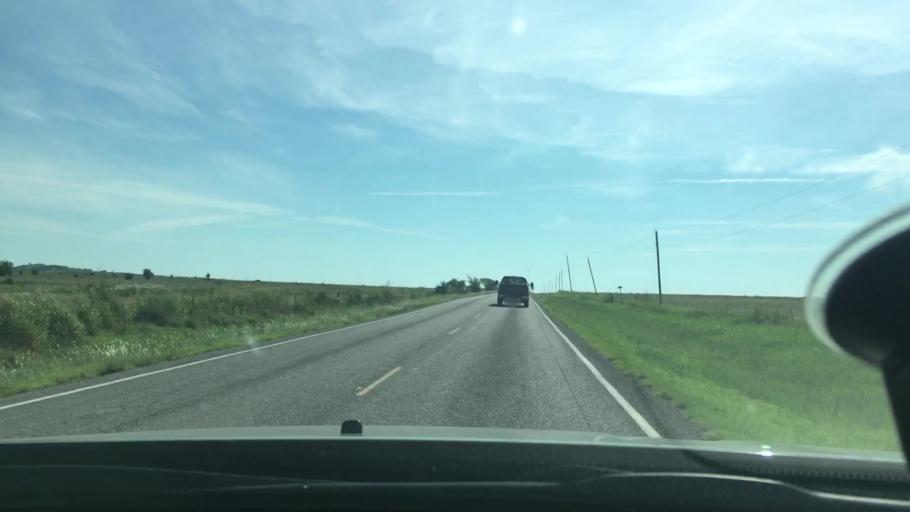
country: US
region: Oklahoma
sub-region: Carter County
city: Lone Grove
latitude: 34.3327
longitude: -97.2601
